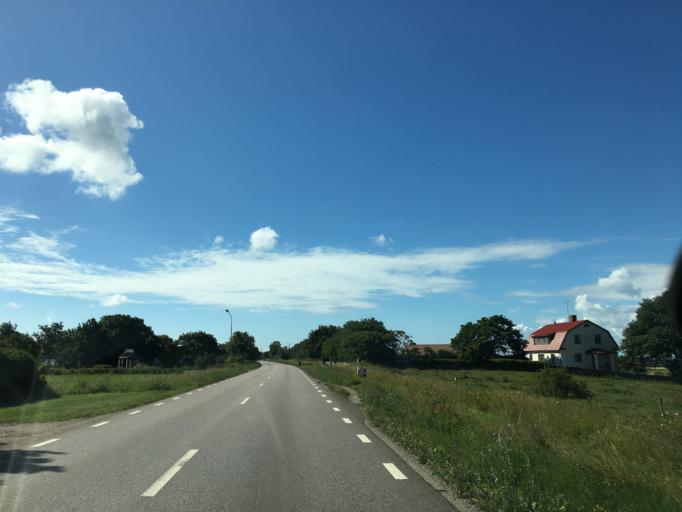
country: SE
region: Kalmar
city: Faerjestaden
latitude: 56.5901
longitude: 16.4654
